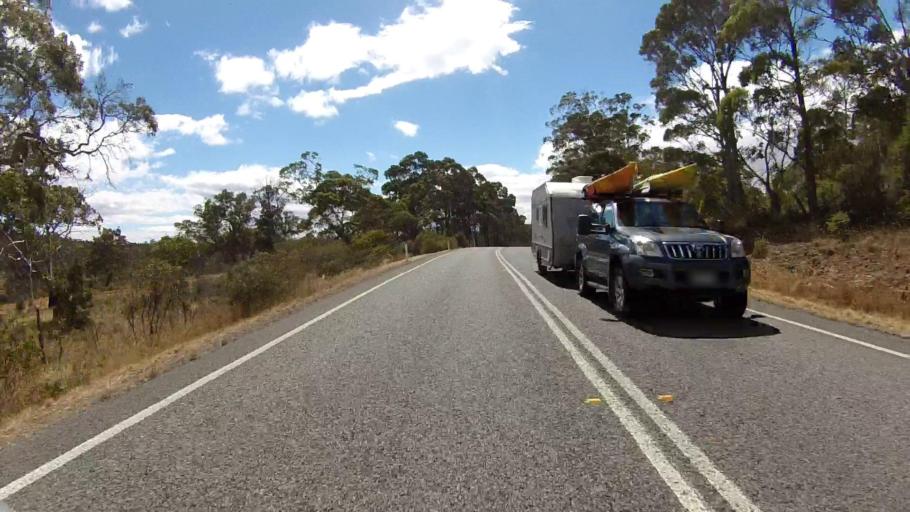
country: AU
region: Tasmania
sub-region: Sorell
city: Sorell
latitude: -42.6208
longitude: 147.6325
